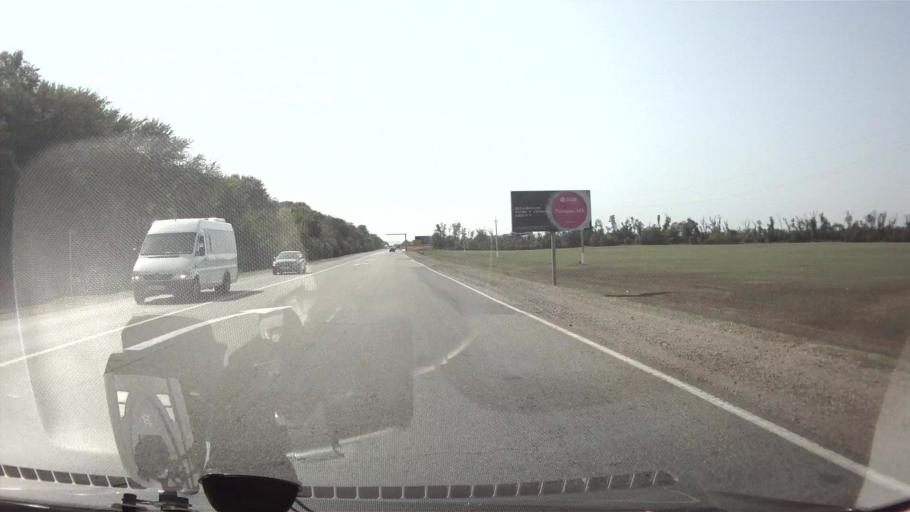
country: RU
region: Krasnodarskiy
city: Vasyurinskaya
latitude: 45.1592
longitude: 39.4582
